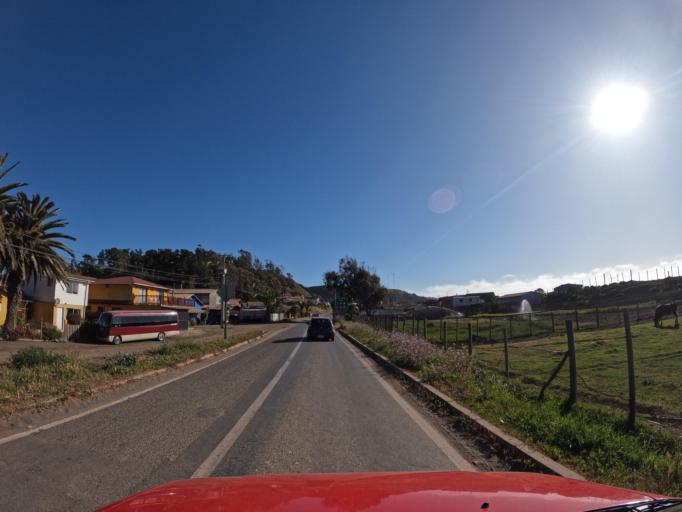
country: CL
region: Maule
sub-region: Provincia de Talca
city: Constitucion
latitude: -34.8808
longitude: -72.1563
